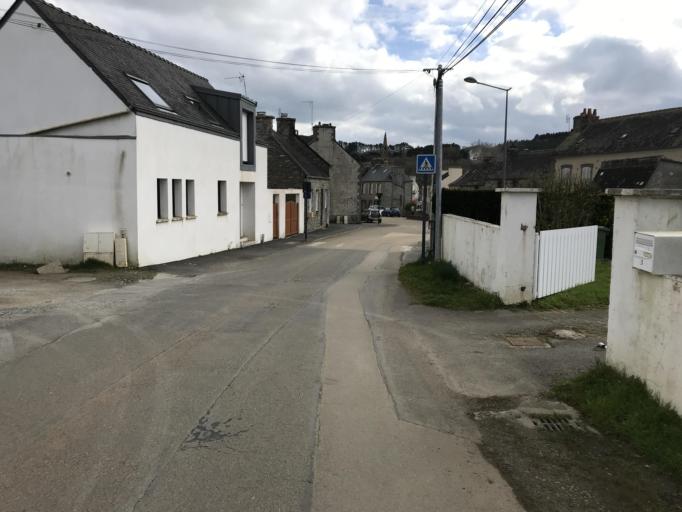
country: FR
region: Brittany
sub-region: Departement du Finistere
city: Hopital-Camfrout
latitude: 48.3301
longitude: -4.2432
